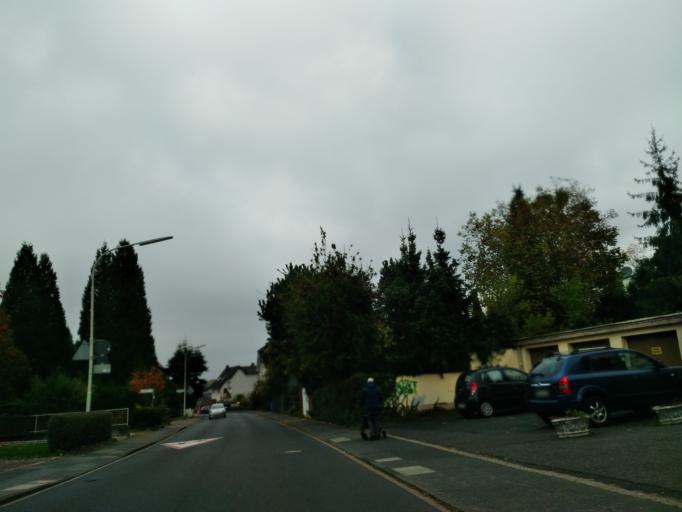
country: DE
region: North Rhine-Westphalia
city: Sankt Augustin
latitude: 50.7426
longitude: 7.1794
